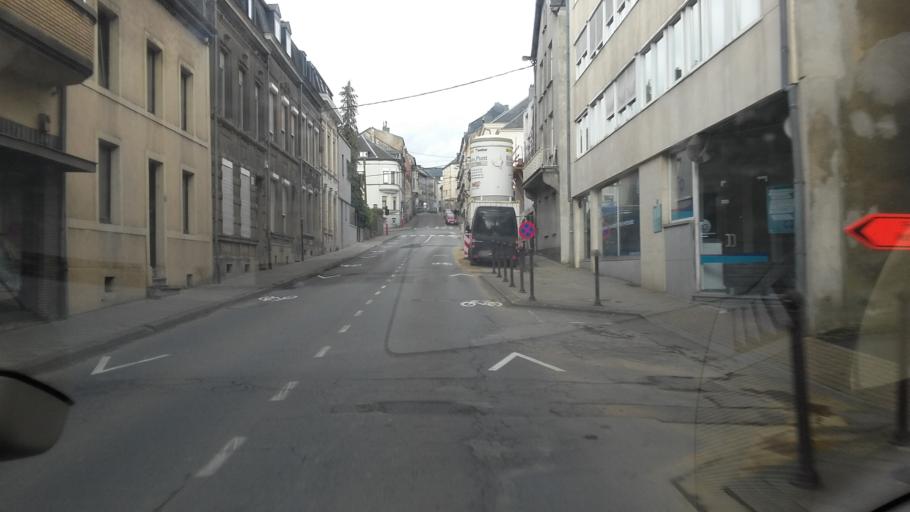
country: BE
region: Wallonia
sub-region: Province du Luxembourg
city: Arlon
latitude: 49.6813
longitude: 5.8188
